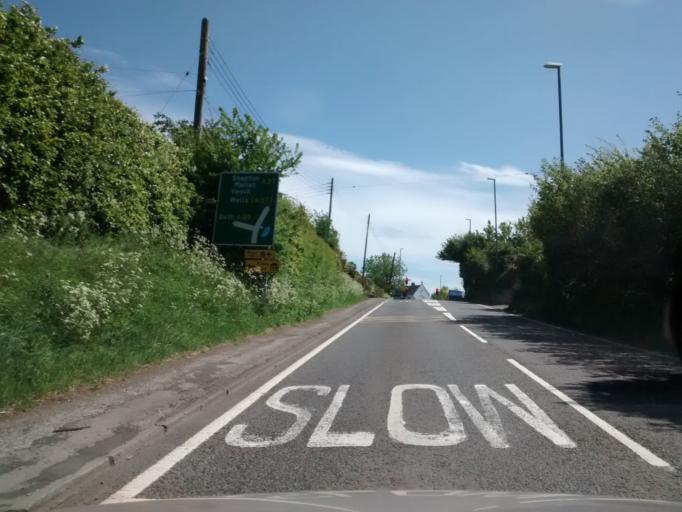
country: GB
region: England
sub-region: Bath and North East Somerset
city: Clutton
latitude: 51.3109
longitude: -2.5344
